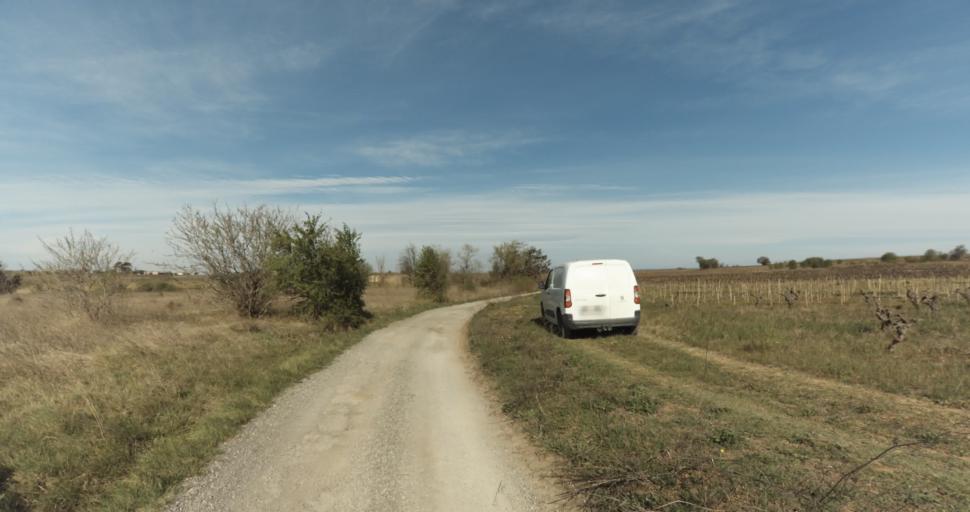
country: FR
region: Languedoc-Roussillon
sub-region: Departement de l'Herault
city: Marseillan
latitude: 43.3504
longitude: 3.4981
